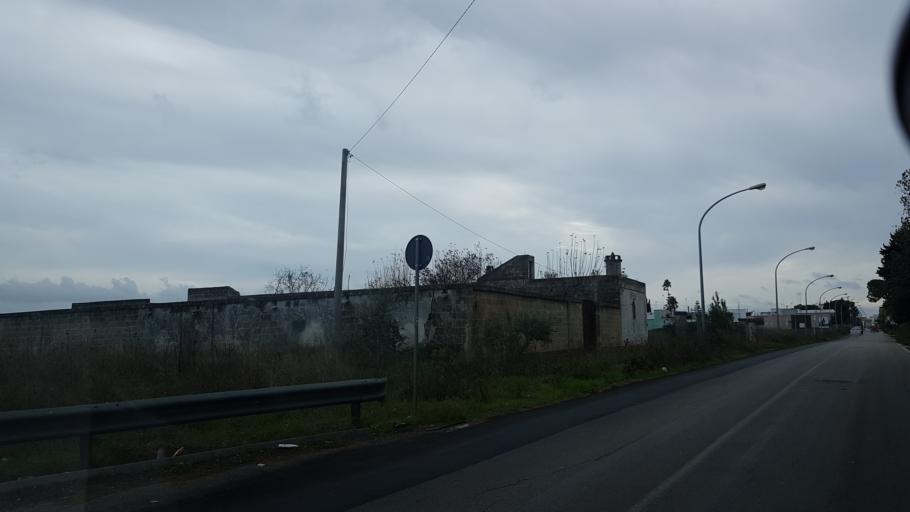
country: IT
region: Apulia
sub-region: Provincia di Brindisi
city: Mesagne
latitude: 40.5687
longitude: 17.7992
